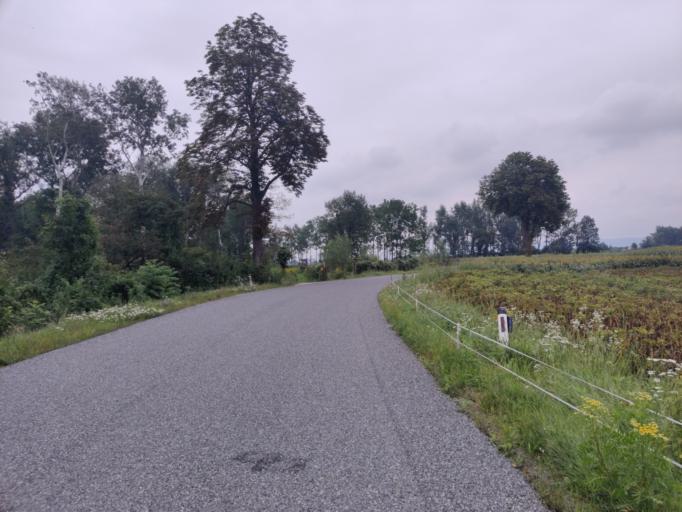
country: AT
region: Lower Austria
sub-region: Politischer Bezirk Tulln
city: Langenrohr
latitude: 48.3262
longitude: 16.0138
